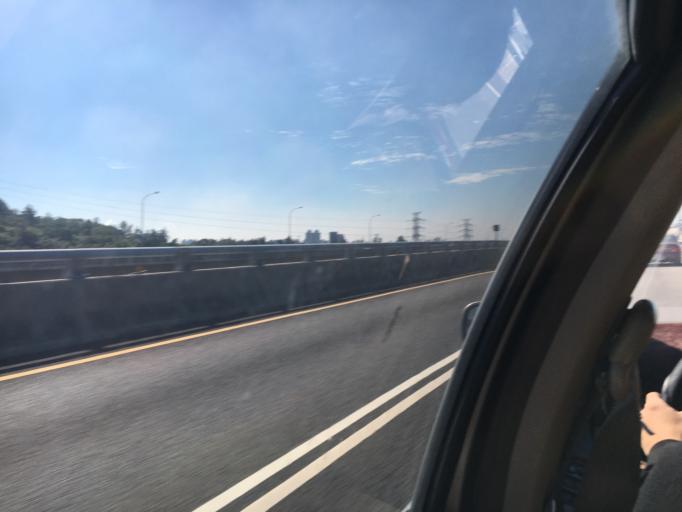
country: TW
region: Taiwan
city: Taoyuan City
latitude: 25.0446
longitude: 121.3104
